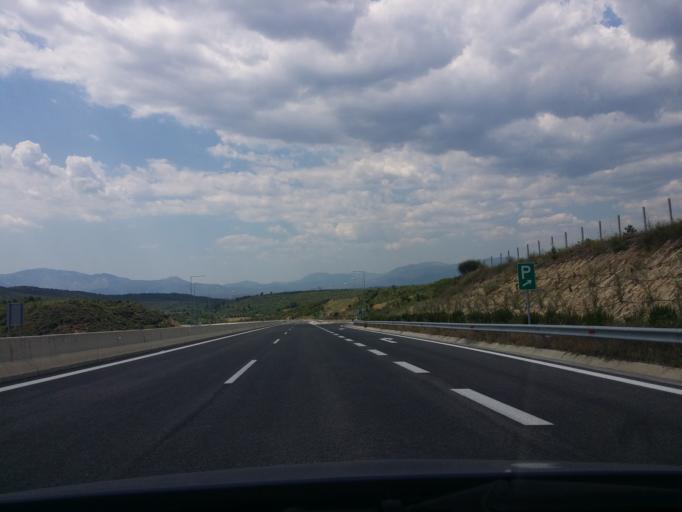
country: GR
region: Peloponnese
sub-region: Nomos Arkadias
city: Megalopoli
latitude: 37.3245
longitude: 22.1652
